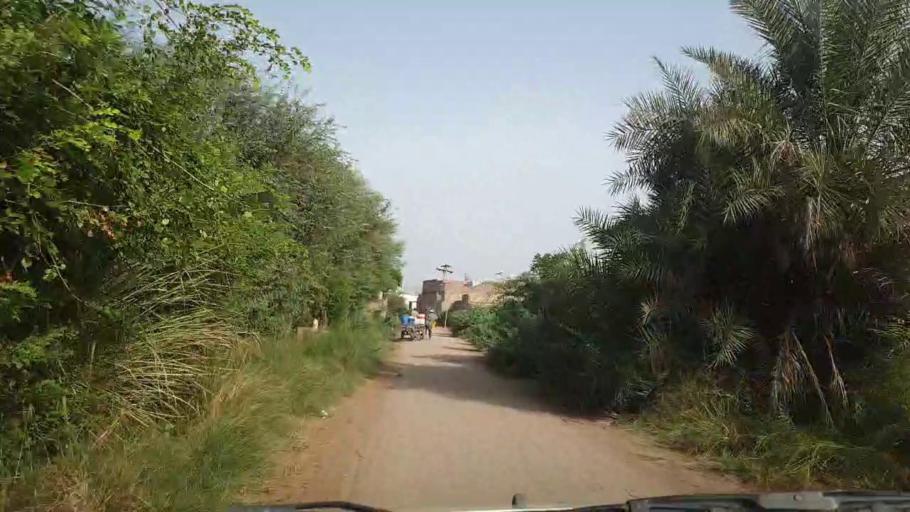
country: PK
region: Sindh
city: Nawabshah
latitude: 26.2327
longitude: 68.4067
